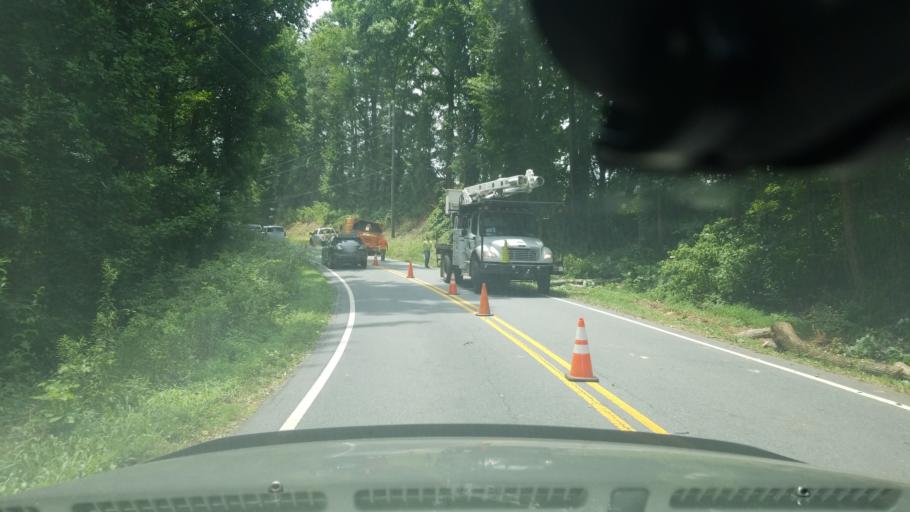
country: US
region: Georgia
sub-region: Forsyth County
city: Cumming
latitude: 34.1935
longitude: -84.2214
